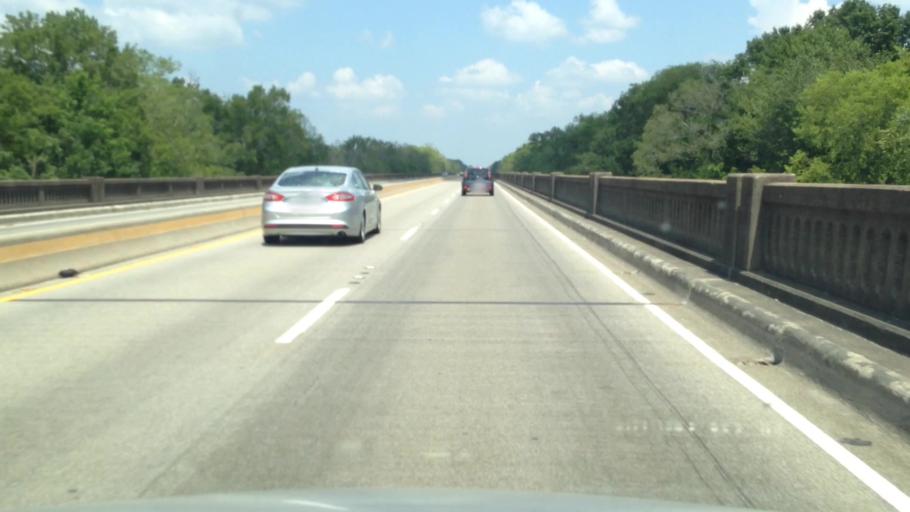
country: US
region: Louisiana
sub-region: Saint Landry Parish
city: Krotz Springs
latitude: 30.5541
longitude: -91.6946
